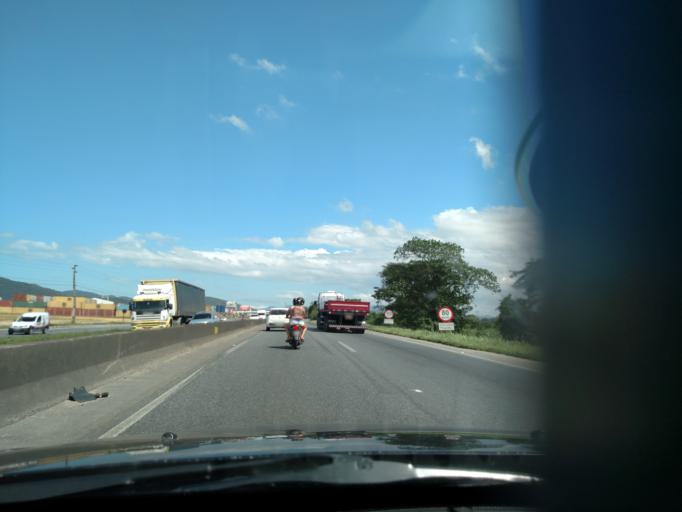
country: BR
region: Santa Catarina
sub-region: Itajai
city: Itajai
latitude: -26.9126
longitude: -48.7121
